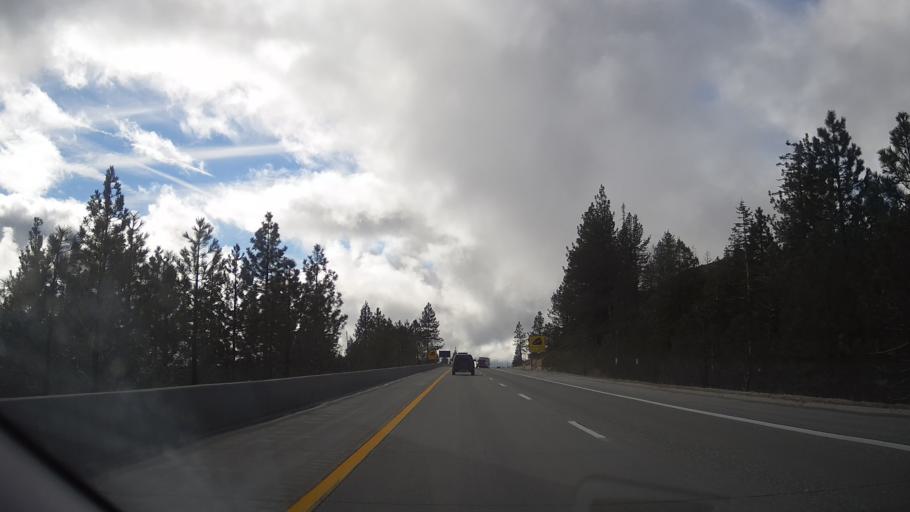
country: US
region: California
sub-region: Sierra County
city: Downieville
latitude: 39.3125
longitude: -120.6303
